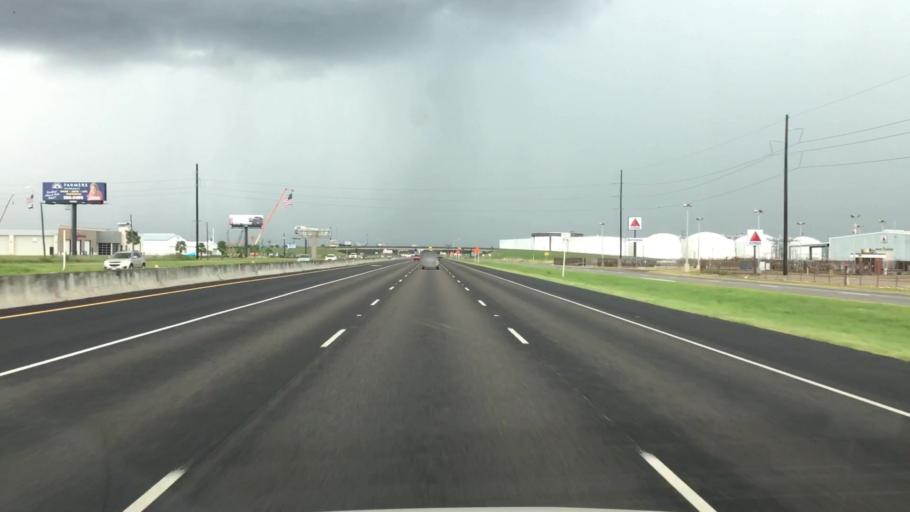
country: US
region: Texas
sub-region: Nueces County
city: Corpus Christi
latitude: 27.8090
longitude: -97.4972
